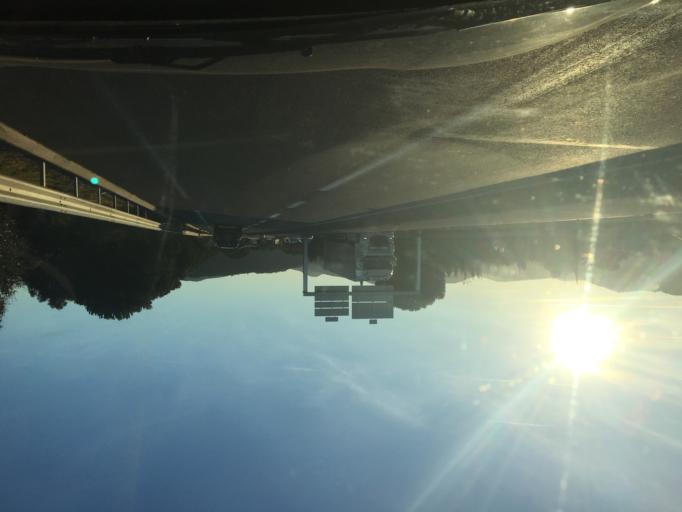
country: FR
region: Provence-Alpes-Cote d'Azur
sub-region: Departement du Var
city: Le Muy
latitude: 43.4660
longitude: 6.5456
